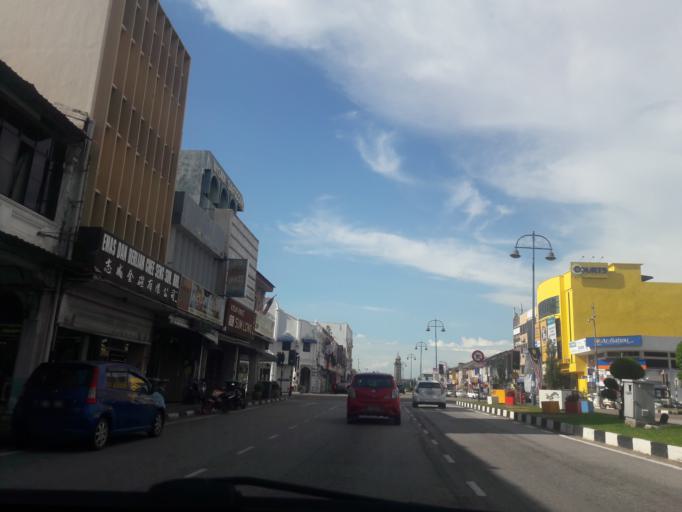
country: MY
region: Kedah
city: Sungai Petani
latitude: 5.6409
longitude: 100.4888
